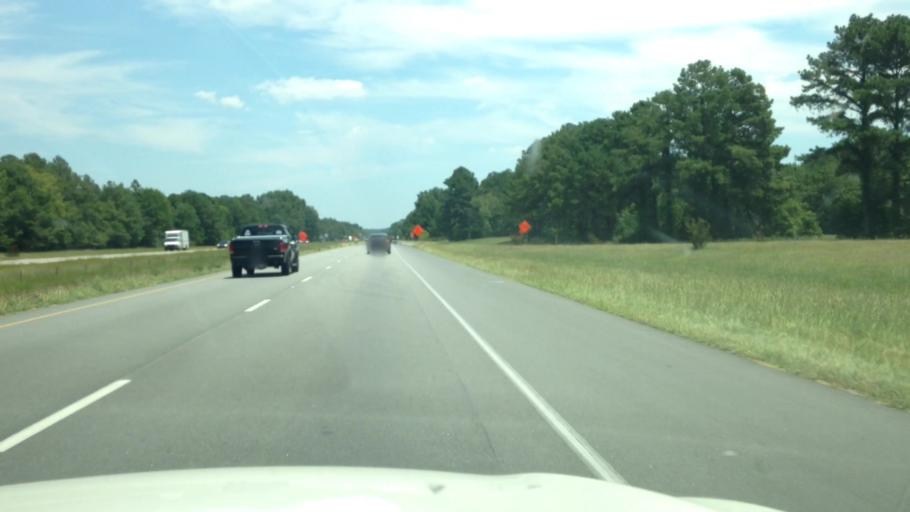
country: US
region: South Carolina
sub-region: Lee County
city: Bishopville
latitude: 34.1864
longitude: -80.2100
